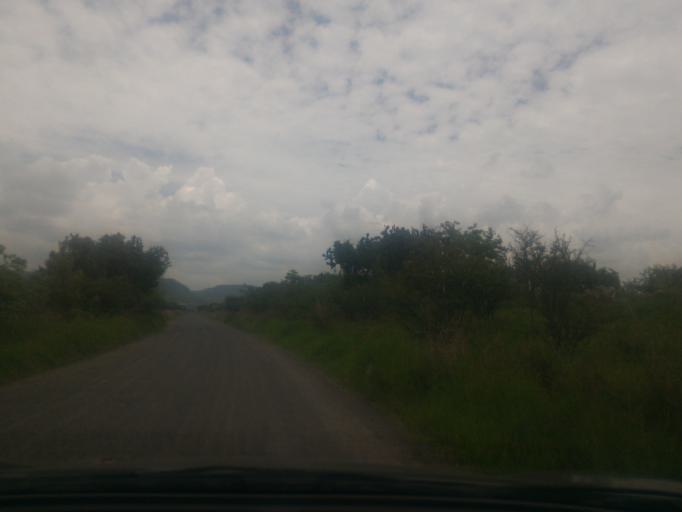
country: MX
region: Guanajuato
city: Ciudad Manuel Doblado
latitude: 20.8190
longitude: -102.0621
